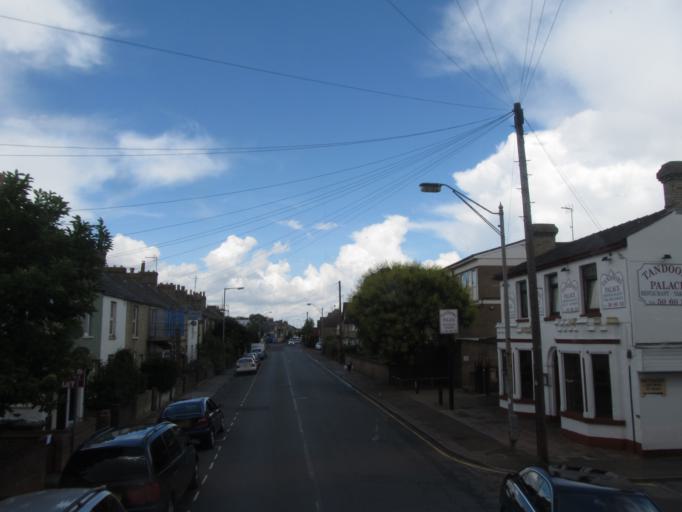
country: GB
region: England
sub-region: Cambridgeshire
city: Cambridge
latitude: 52.2162
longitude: 0.1110
